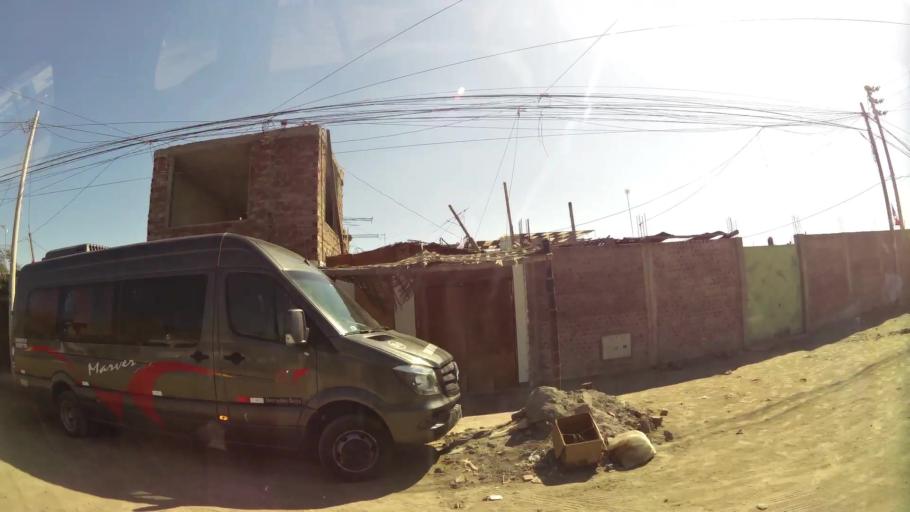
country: PE
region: Ica
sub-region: Provincia de Ica
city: La Tinguina
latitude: -14.0360
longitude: -75.7017
